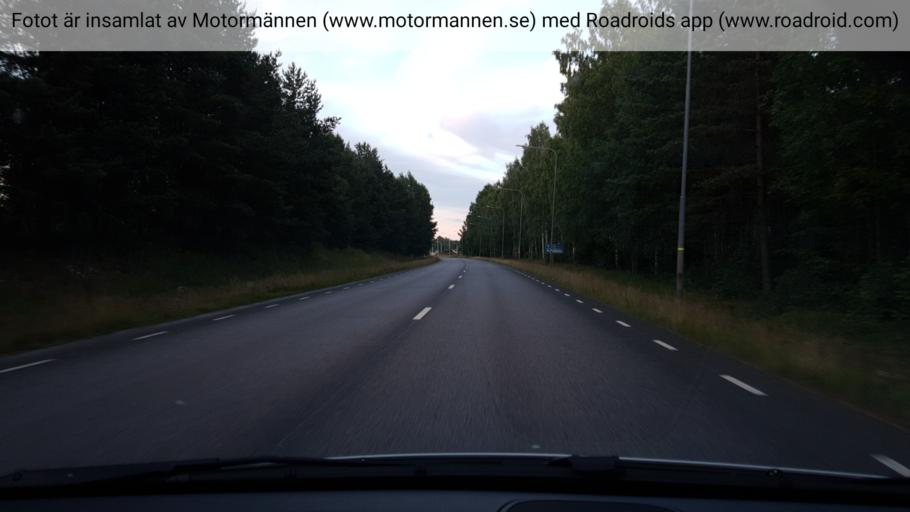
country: SE
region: Vaestra Goetaland
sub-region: Tibro Kommun
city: Tibro
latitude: 58.4098
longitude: 14.1804
